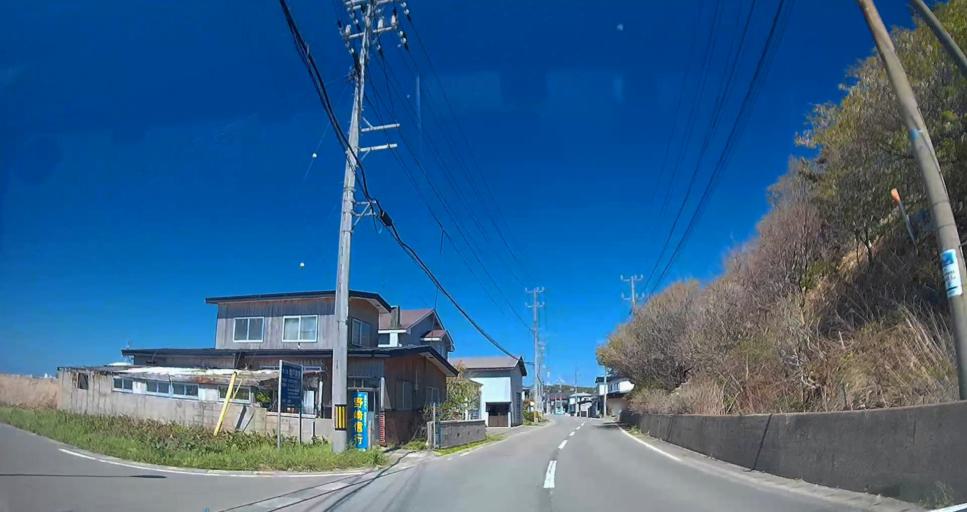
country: JP
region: Hokkaido
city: Hakodate
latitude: 41.5013
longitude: 140.9092
